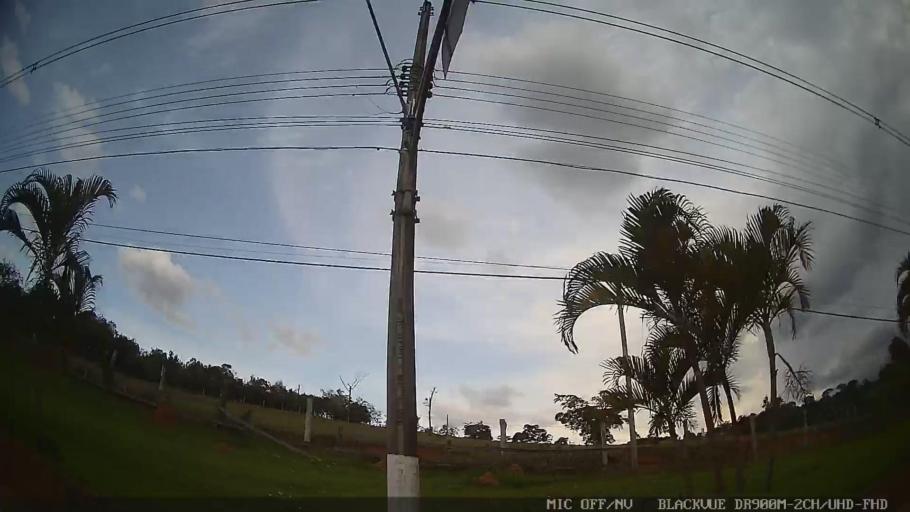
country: BR
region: Sao Paulo
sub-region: Itatiba
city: Itatiba
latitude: -22.8871
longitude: -46.7913
